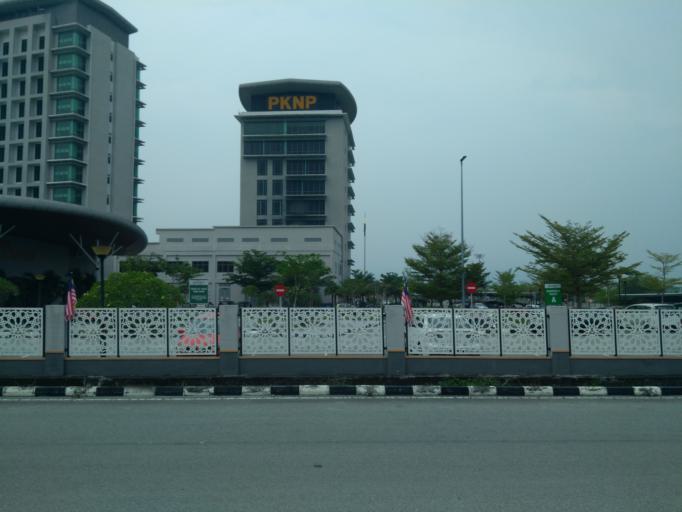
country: MY
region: Perak
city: Ipoh
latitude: 4.6670
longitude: 101.0772
